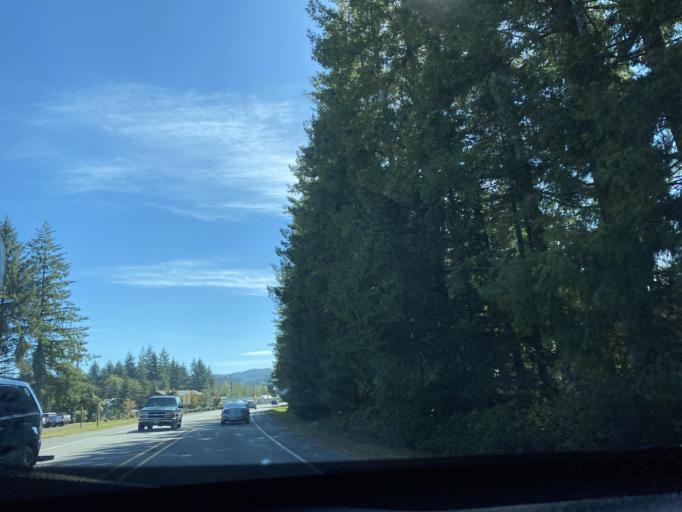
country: US
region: Washington
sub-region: Clallam County
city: Forks
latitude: 47.9556
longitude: -124.3862
